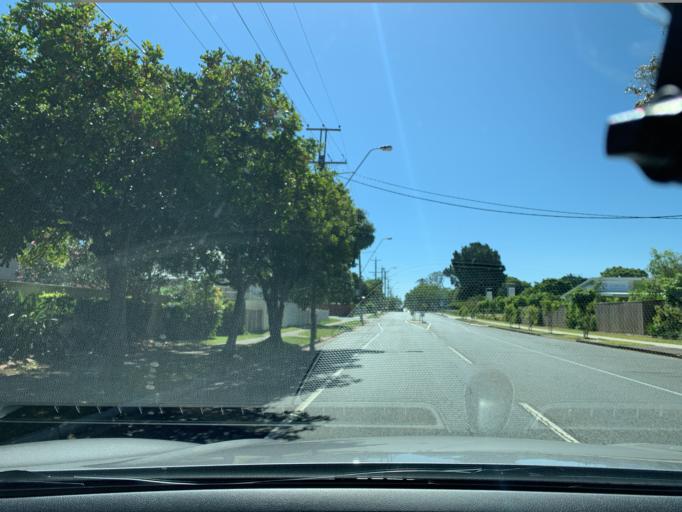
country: AU
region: Queensland
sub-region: Brisbane
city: Ascot
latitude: -27.4317
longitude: 153.0696
